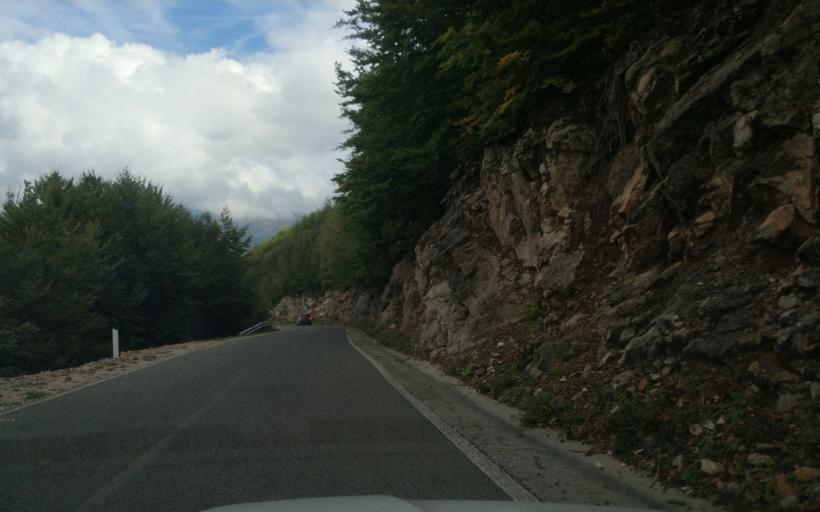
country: AL
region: Durres
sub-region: Rrethi i Krujes
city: Kruje
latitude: 41.5225
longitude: 19.8067
